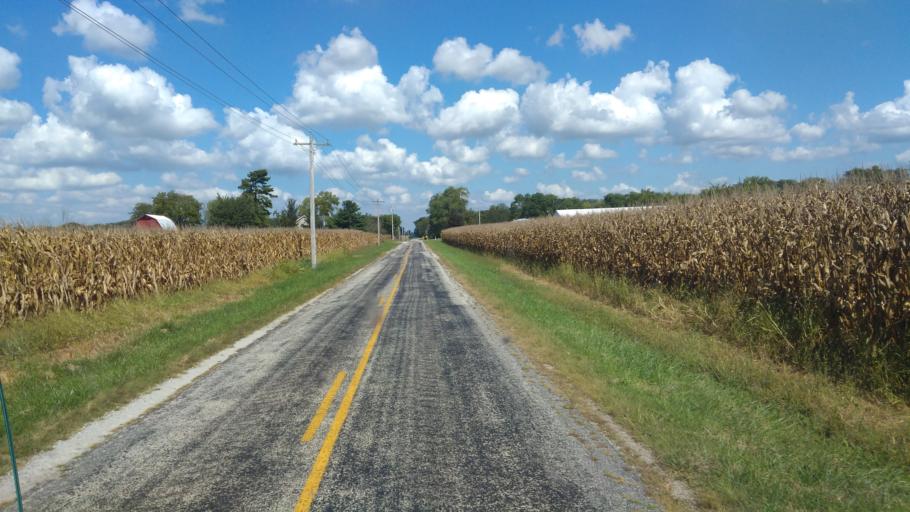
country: US
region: Ohio
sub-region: Wyandot County
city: Upper Sandusky
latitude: 40.6671
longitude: -83.3430
